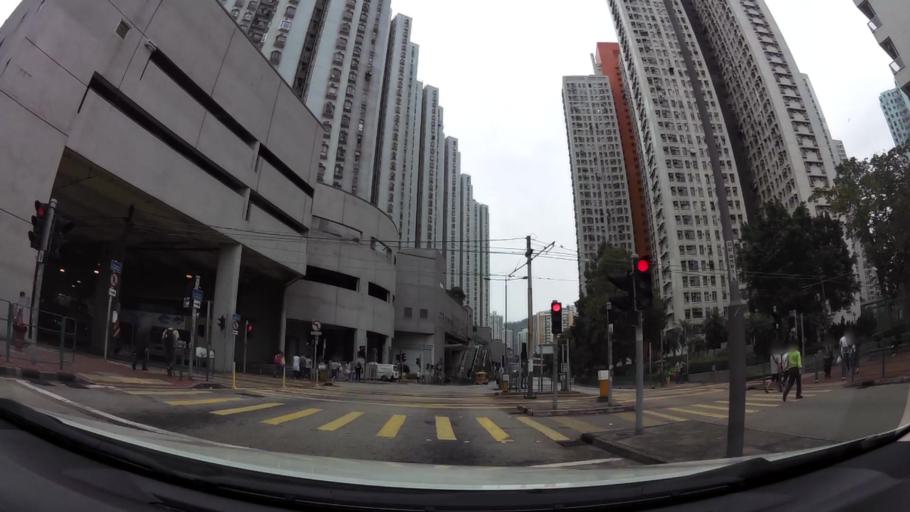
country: HK
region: Tuen Mun
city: Tuen Mun
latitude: 22.3726
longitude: 113.9682
